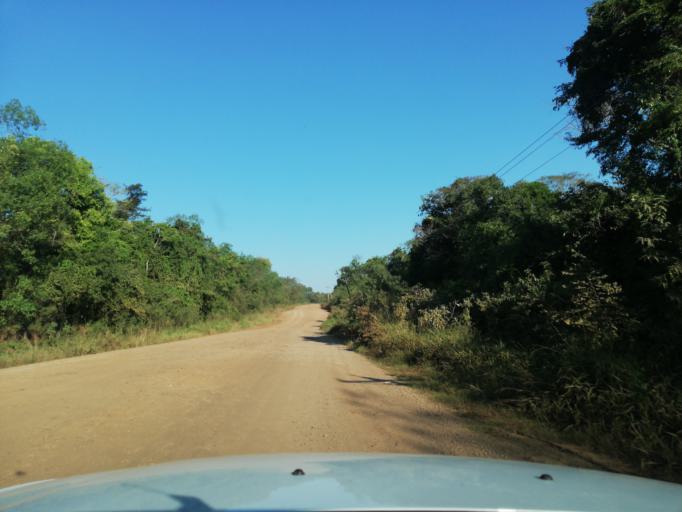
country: AR
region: Misiones
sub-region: Departamento de Candelaria
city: Candelaria
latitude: -27.5530
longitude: -55.7084
